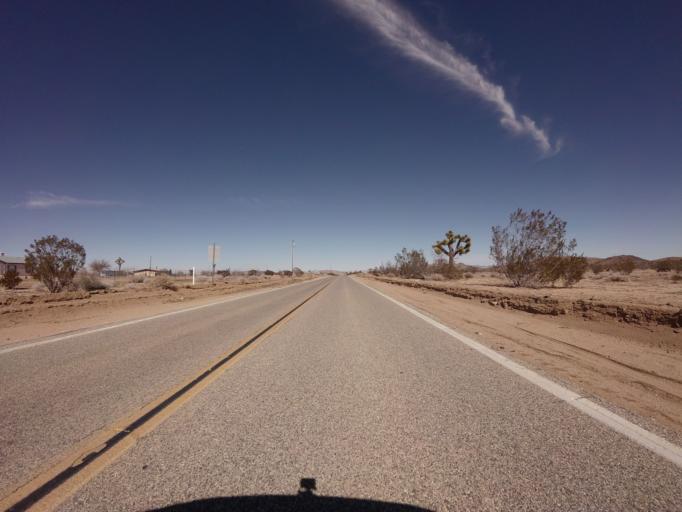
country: US
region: California
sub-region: San Bernardino County
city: Yucca Valley
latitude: 34.2416
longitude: -116.3933
